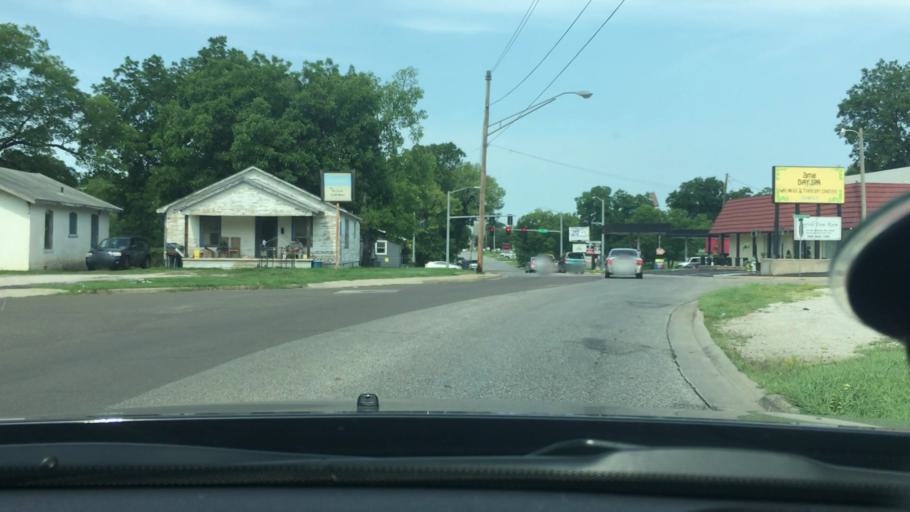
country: US
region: Oklahoma
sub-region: Carter County
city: Ardmore
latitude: 34.1866
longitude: -97.1365
